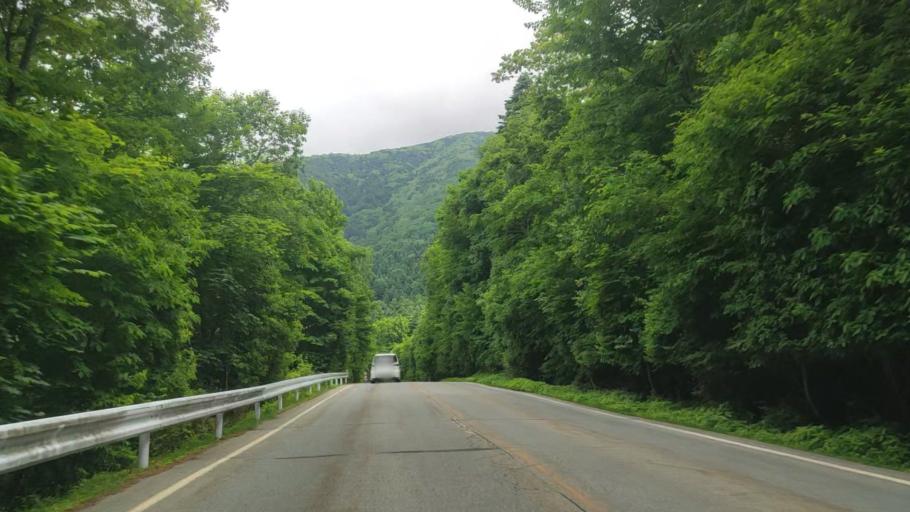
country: JP
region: Yamanashi
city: Fujikawaguchiko
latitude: 35.4160
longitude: 138.7384
